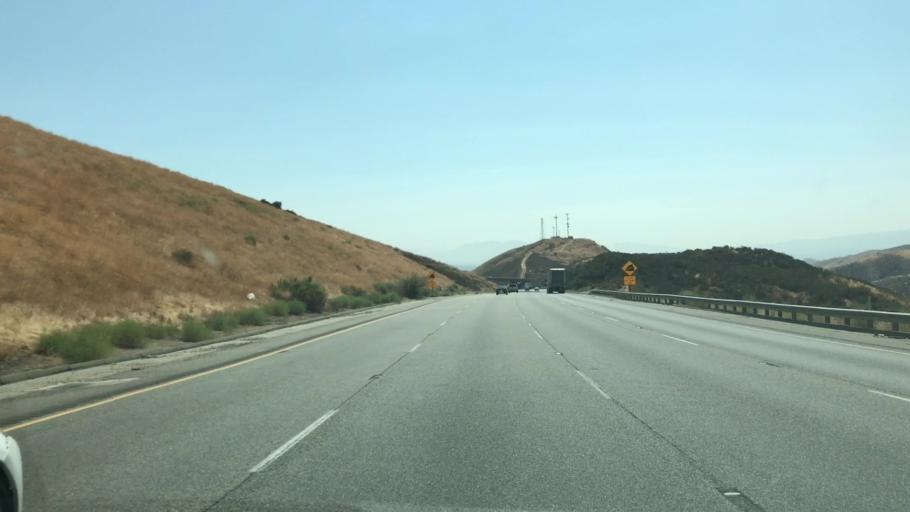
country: US
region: California
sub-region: Los Angeles County
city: Castaic
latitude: 34.5576
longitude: -118.6761
